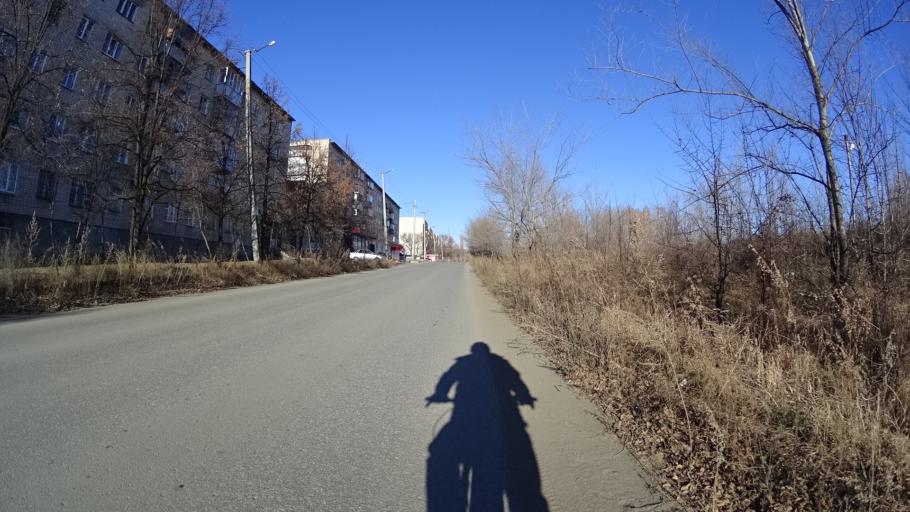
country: RU
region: Chelyabinsk
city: Troitsk
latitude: 54.0501
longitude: 61.6406
